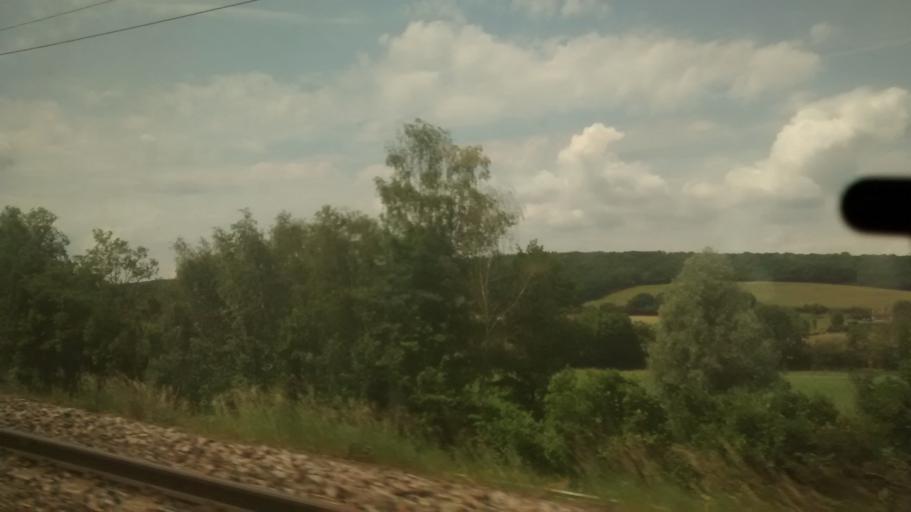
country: FR
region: Bourgogne
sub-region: Departement de Saone-et-Loire
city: Cluny
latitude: 46.4131
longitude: 4.6602
